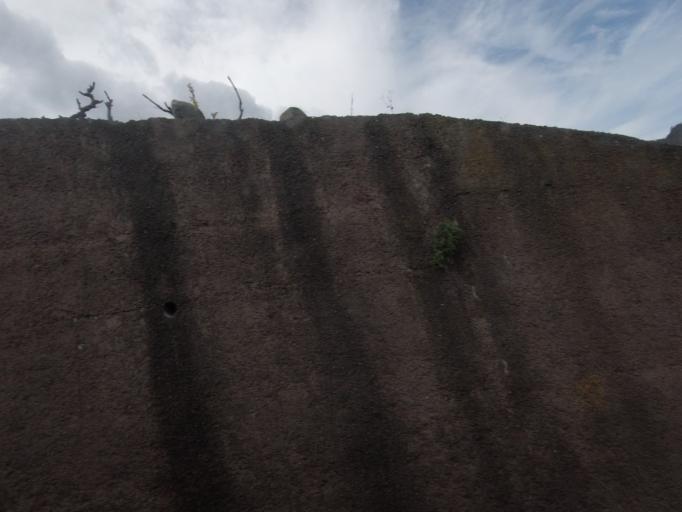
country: PT
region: Madeira
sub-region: Santana
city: Santana
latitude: 32.7640
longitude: -16.8275
